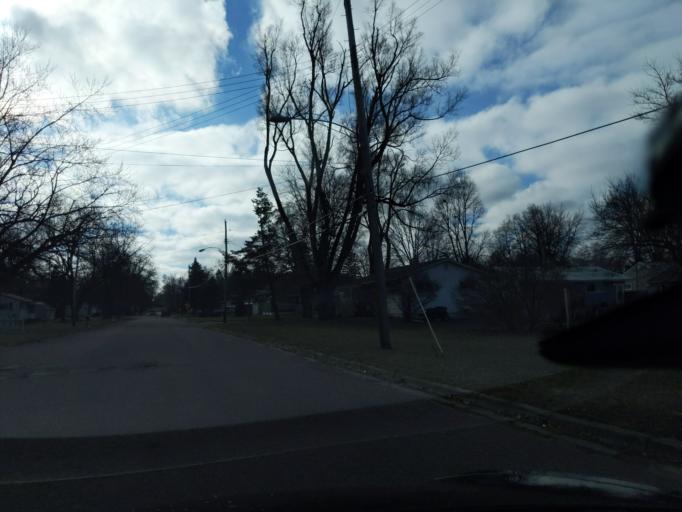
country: US
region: Michigan
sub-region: Ingham County
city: Lansing
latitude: 42.6945
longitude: -84.5773
